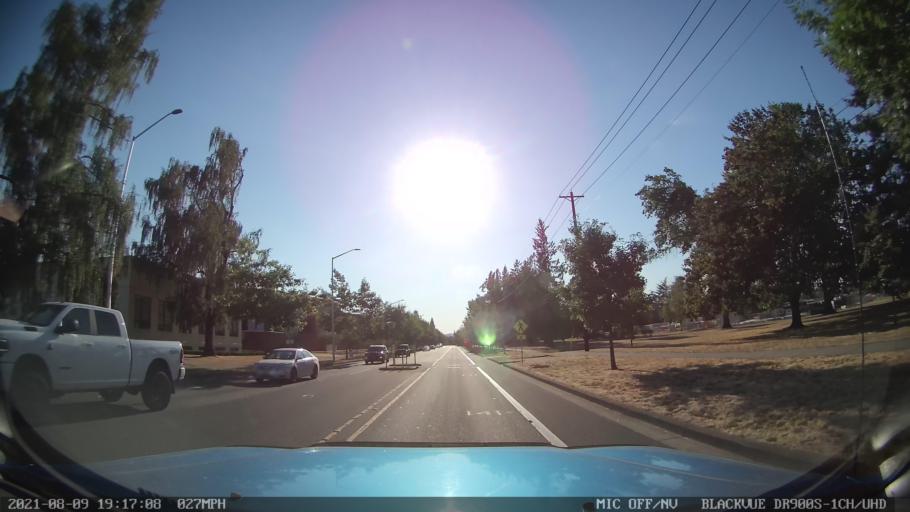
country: US
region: Oregon
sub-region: Marion County
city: Four Corners
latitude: 44.9399
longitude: -123.0005
